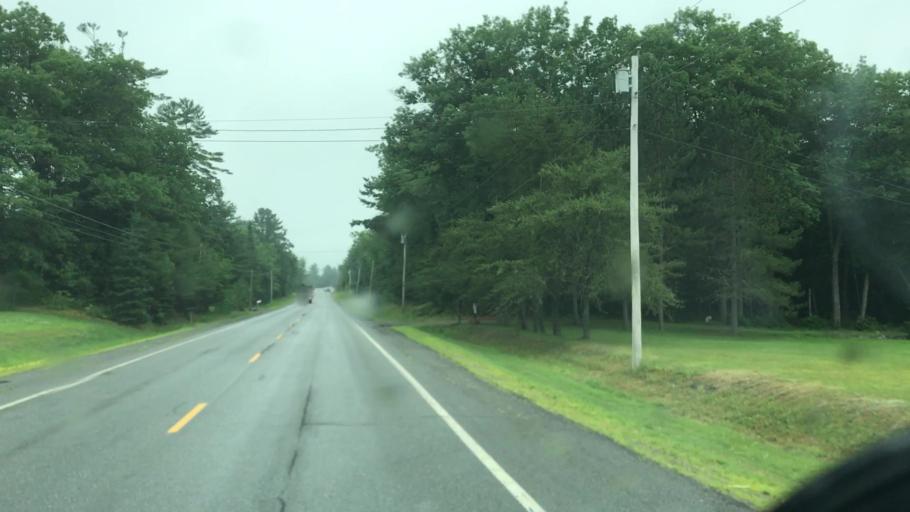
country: US
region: Maine
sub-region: Penobscot County
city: Howland
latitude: 45.2933
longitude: -68.6217
